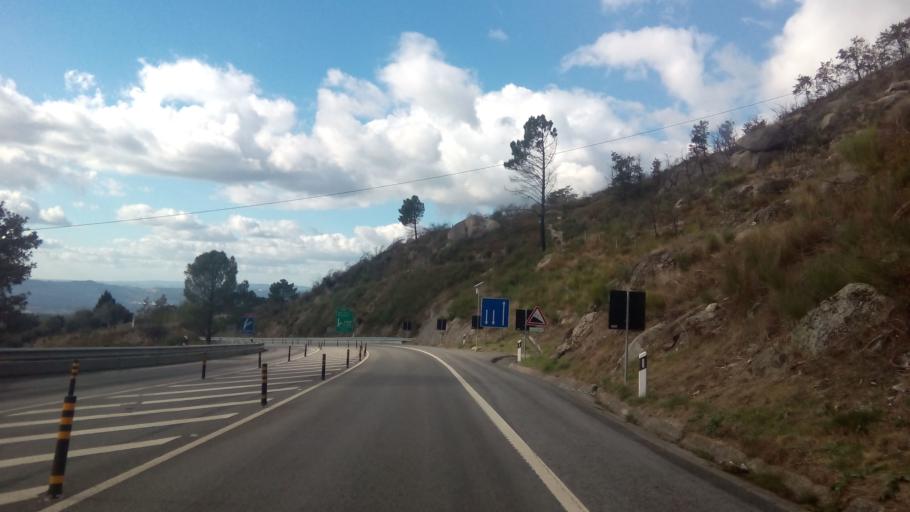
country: PT
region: Porto
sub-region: Baiao
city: Valadares
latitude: 41.2555
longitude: -7.9598
